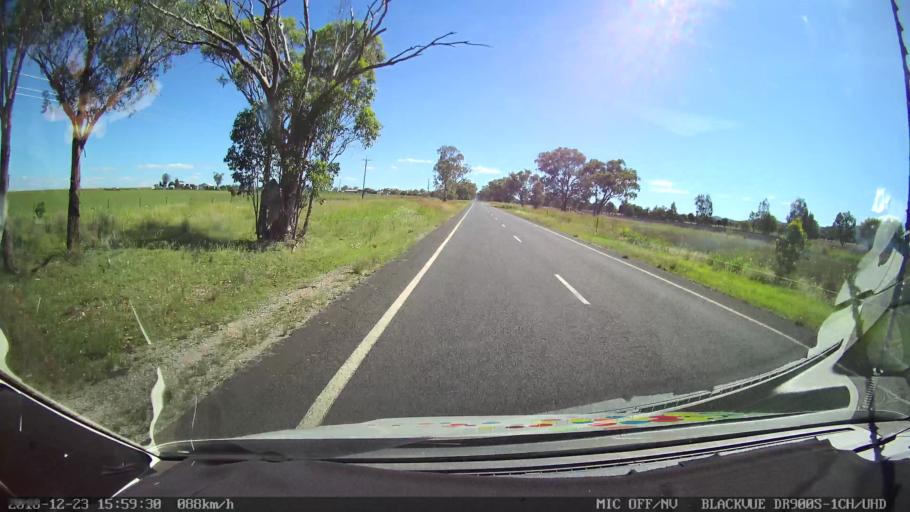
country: AU
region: New South Wales
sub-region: Tamworth Municipality
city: Phillip
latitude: -31.2005
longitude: 150.8326
